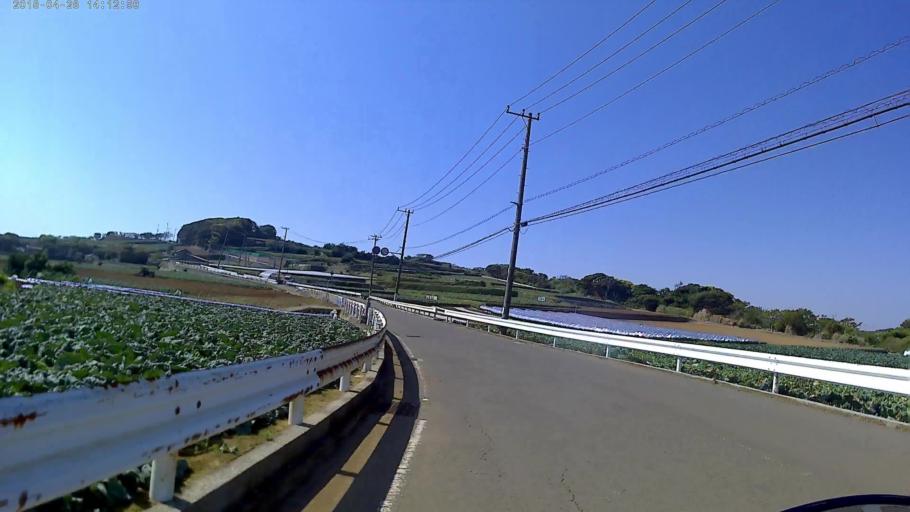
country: JP
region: Kanagawa
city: Miura
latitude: 35.1487
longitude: 139.6511
